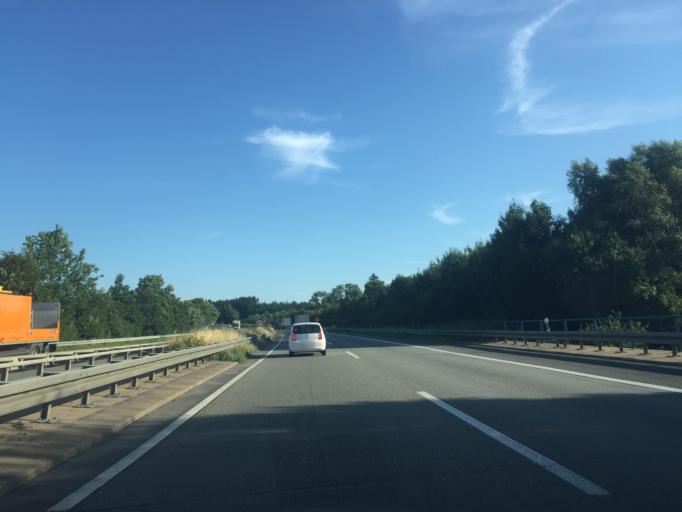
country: DE
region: North Rhine-Westphalia
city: Meinerzhagen
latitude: 51.1432
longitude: 7.6758
